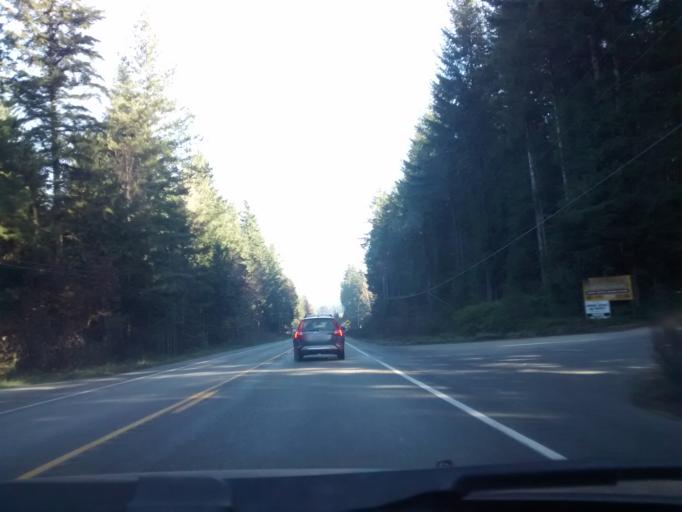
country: US
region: Washington
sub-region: Kitsap County
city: Lofall
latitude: 47.8072
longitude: -122.6478
